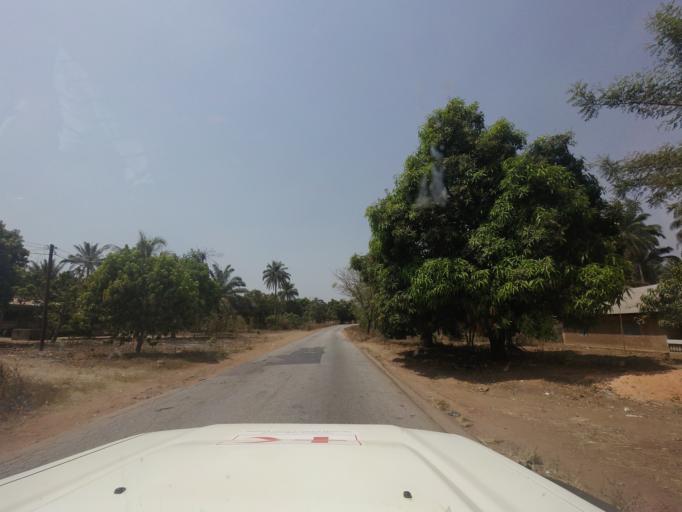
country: GN
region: Kindia
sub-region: Kindia
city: Kindia
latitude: 9.9615
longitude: -12.9394
